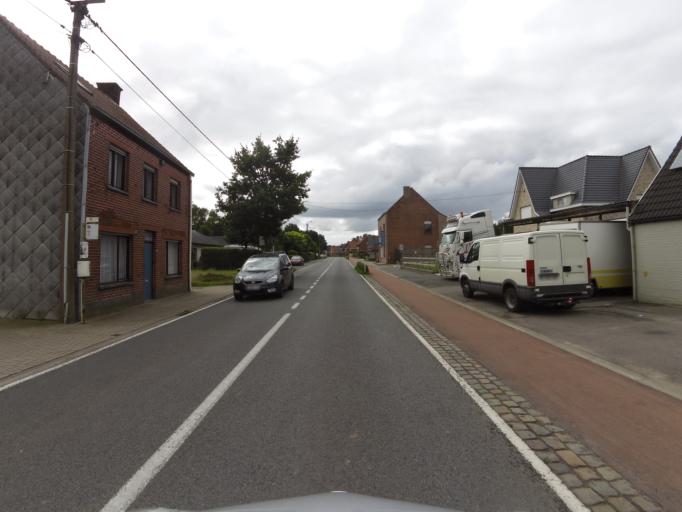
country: BE
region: Flanders
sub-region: Provincie West-Vlaanderen
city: Torhout
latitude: 51.0856
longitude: 3.0987
